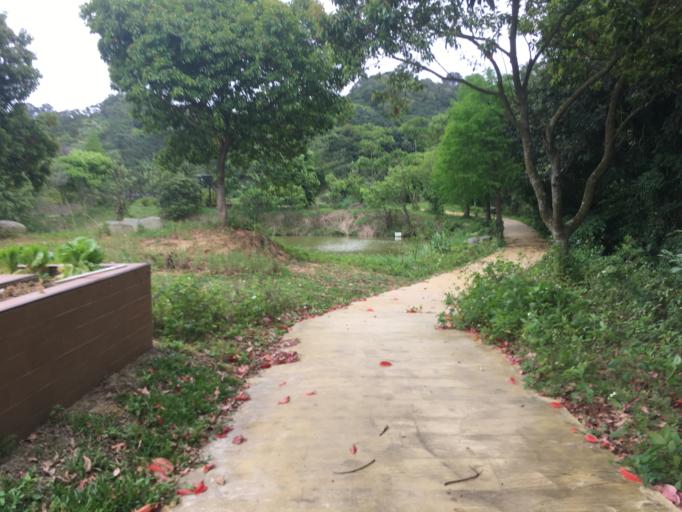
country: TW
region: Taiwan
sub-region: Hsinchu
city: Hsinchu
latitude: 24.7413
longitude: 120.9770
